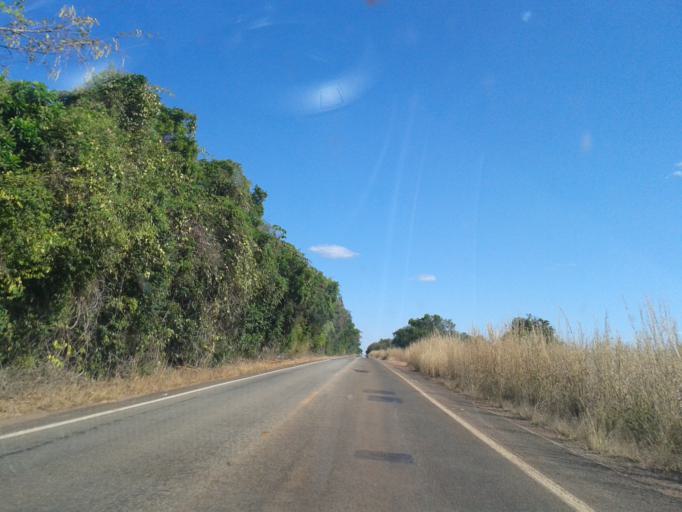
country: BR
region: Goias
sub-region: Mozarlandia
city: Mozarlandia
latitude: -14.4380
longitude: -50.4575
